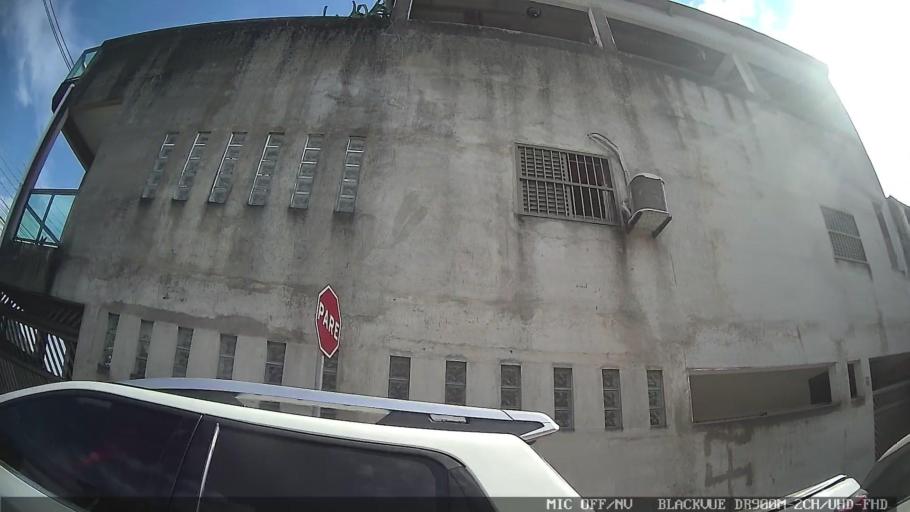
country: BR
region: Sao Paulo
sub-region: Guaruja
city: Guaruja
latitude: -23.9652
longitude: -46.2520
